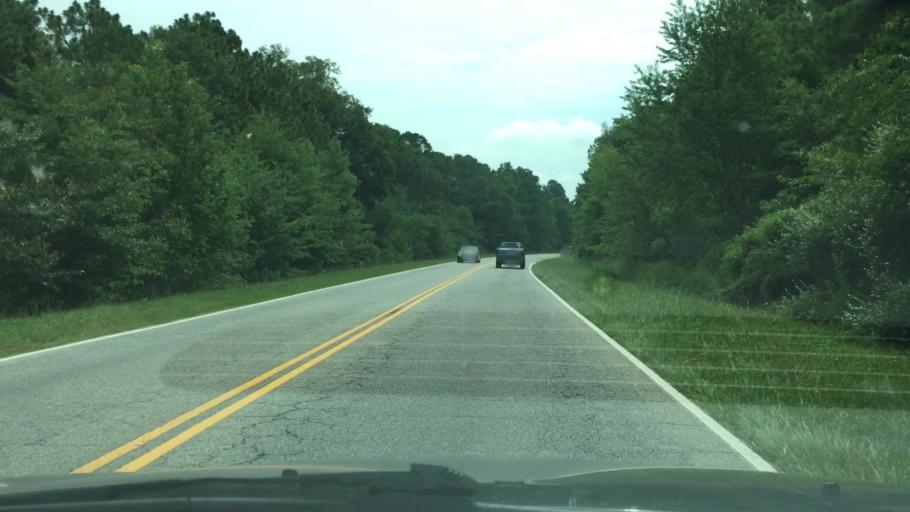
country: US
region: South Carolina
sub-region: Aiken County
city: Aiken
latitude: 33.5296
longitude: -81.7583
